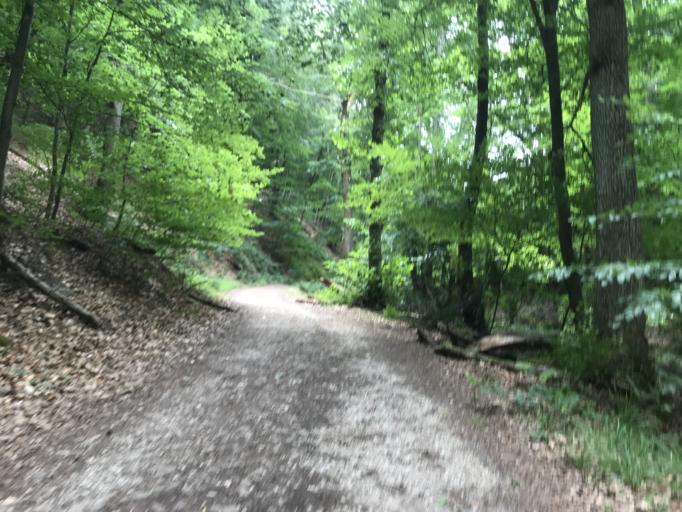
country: DE
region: Rheinland-Pfalz
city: Trechtingshausen
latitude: 49.9889
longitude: 7.8457
